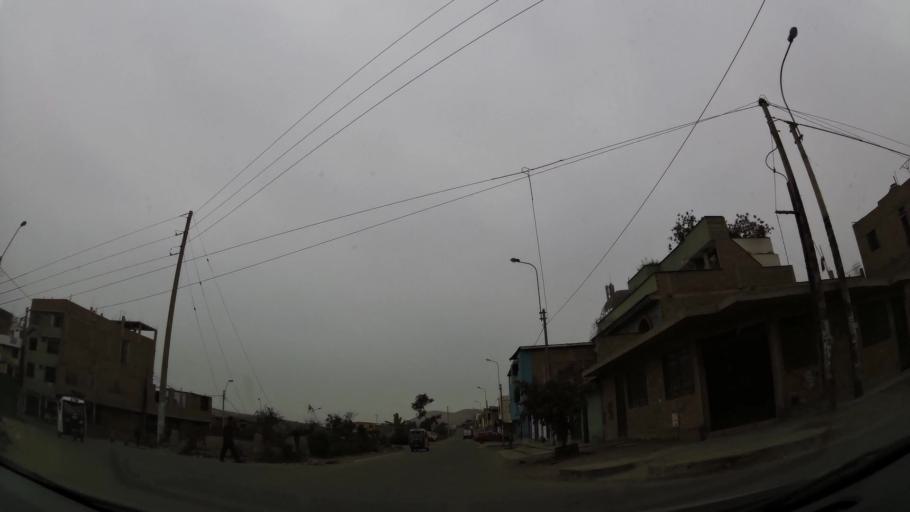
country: PE
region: Lima
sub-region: Lima
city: Surco
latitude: -12.1799
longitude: -76.9812
